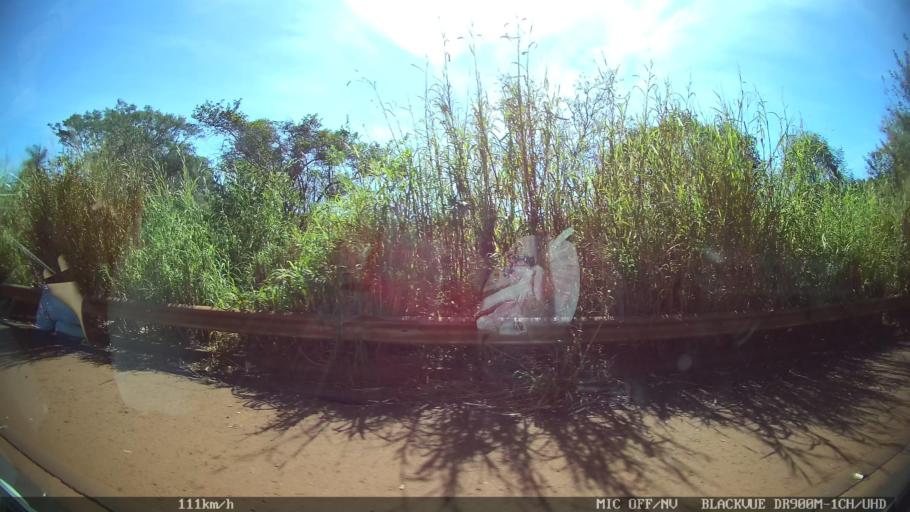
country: BR
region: Sao Paulo
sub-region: Sao Joaquim Da Barra
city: Sao Joaquim da Barra
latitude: -20.5525
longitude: -47.6620
